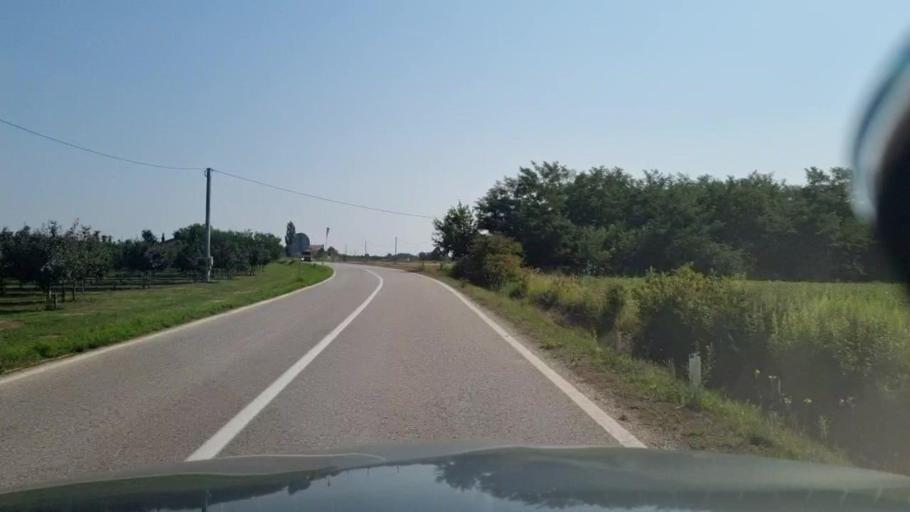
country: BA
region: Federation of Bosnia and Herzegovina
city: Mionica
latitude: 44.8758
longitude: 18.5197
